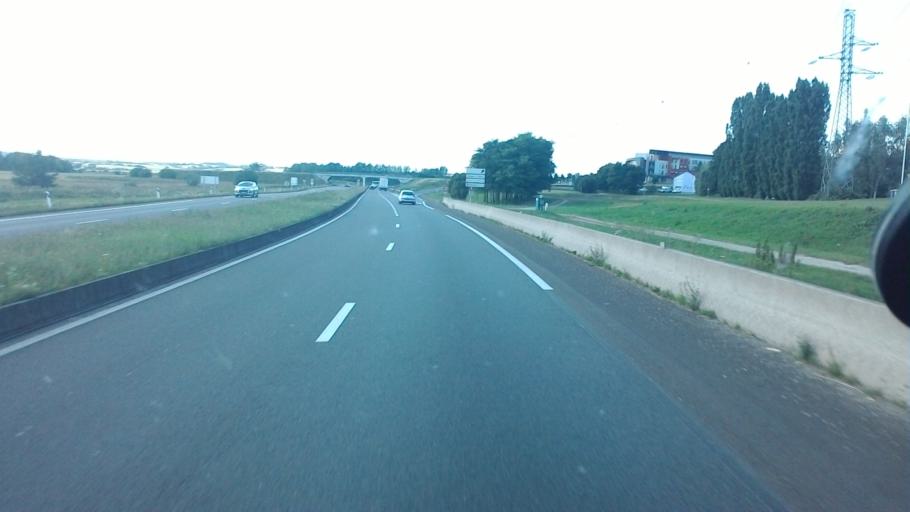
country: FR
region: Franche-Comte
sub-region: Departement de la Haute-Saone
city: Noidans-les-Vesoul
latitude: 47.6318
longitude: 6.1382
